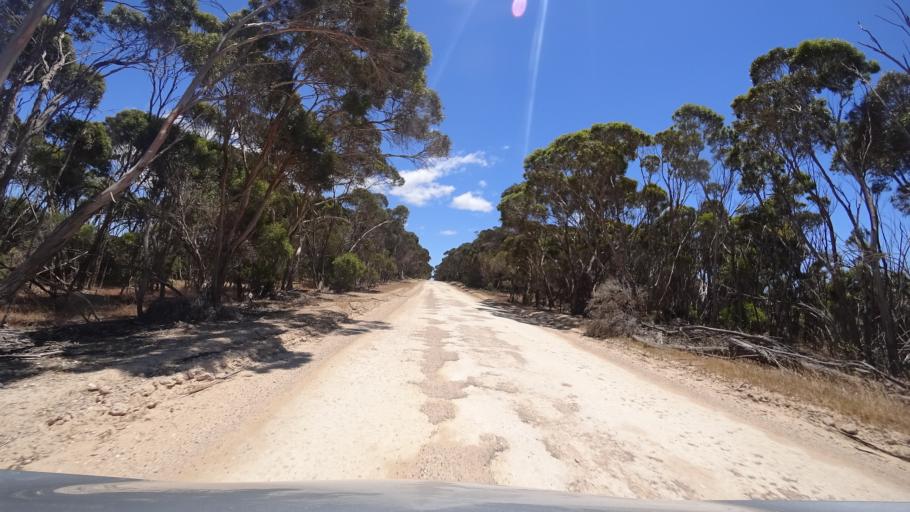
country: AU
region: South Australia
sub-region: Yankalilla
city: Normanville
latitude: -35.8230
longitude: 138.0799
